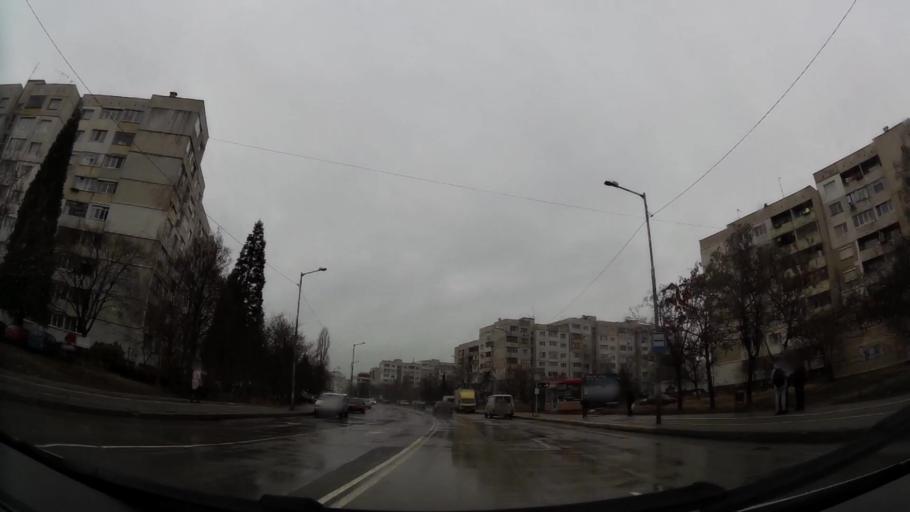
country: BG
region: Sofia-Capital
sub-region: Stolichna Obshtina
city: Sofia
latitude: 42.6371
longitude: 23.3806
